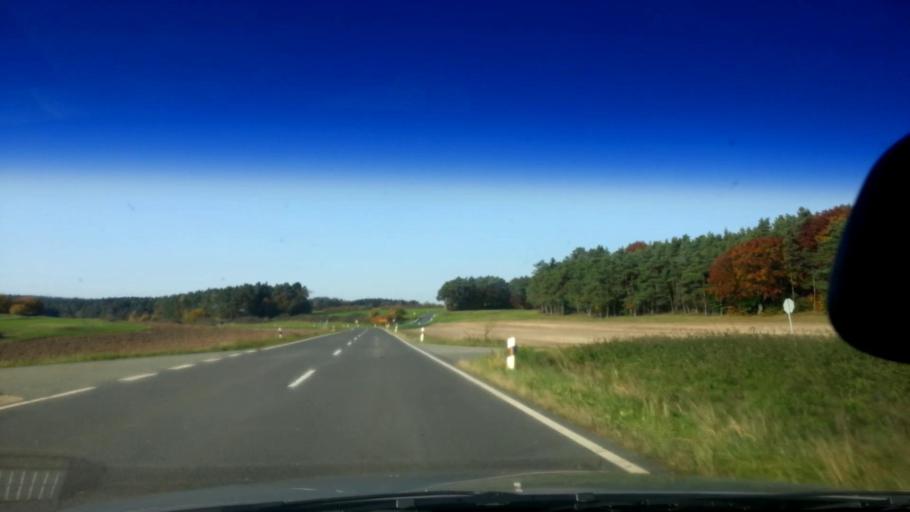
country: DE
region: Bavaria
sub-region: Upper Franconia
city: Konigsfeld
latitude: 49.9806
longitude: 11.1469
